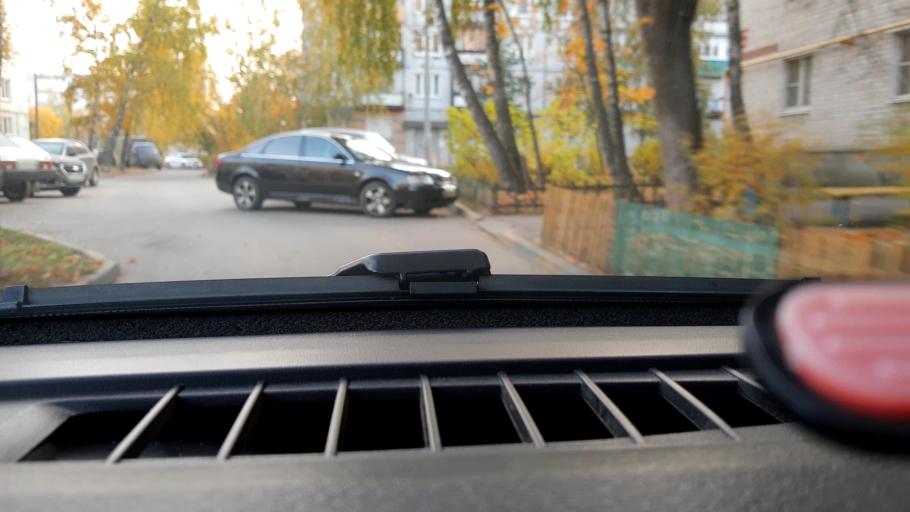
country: RU
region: Nizjnij Novgorod
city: Gorbatovka
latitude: 56.3462
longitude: 43.8020
